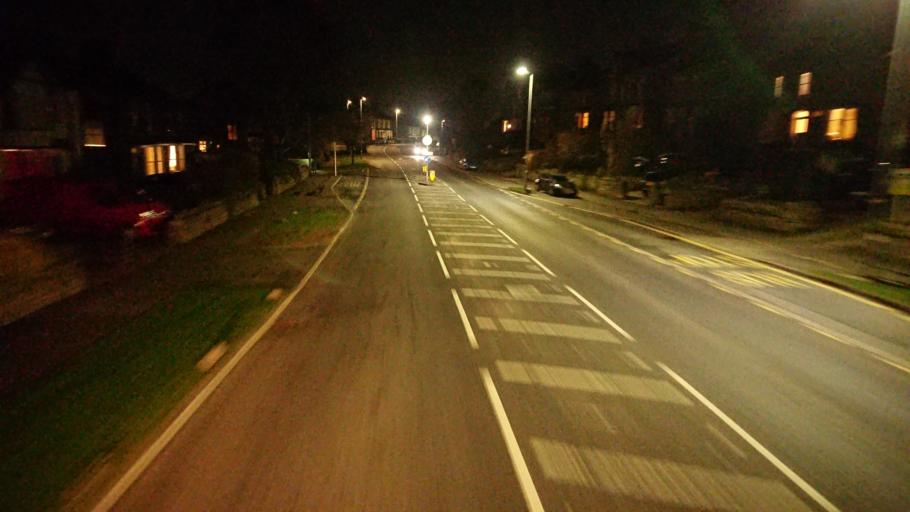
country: GB
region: England
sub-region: Cumbria
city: Kendal
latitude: 54.3352
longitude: -2.7579
